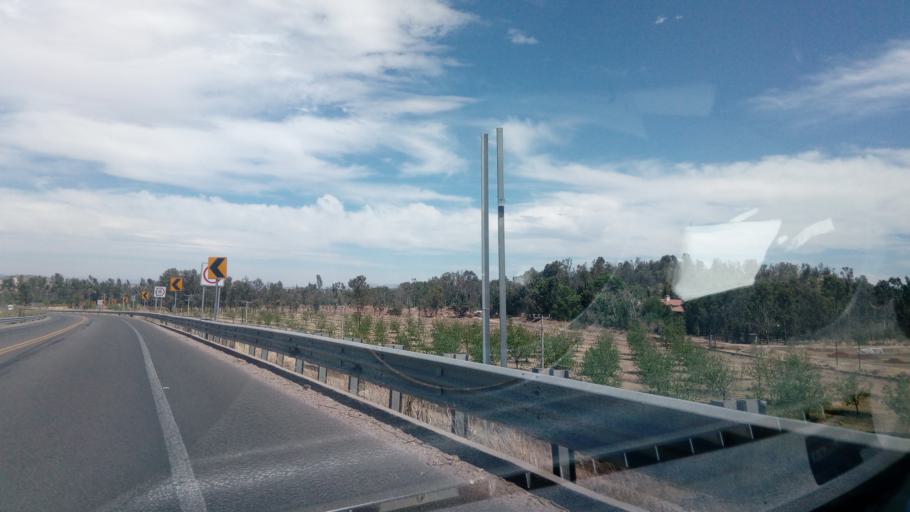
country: MX
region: Durango
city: Victoria de Durango
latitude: 24.0695
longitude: -104.6532
